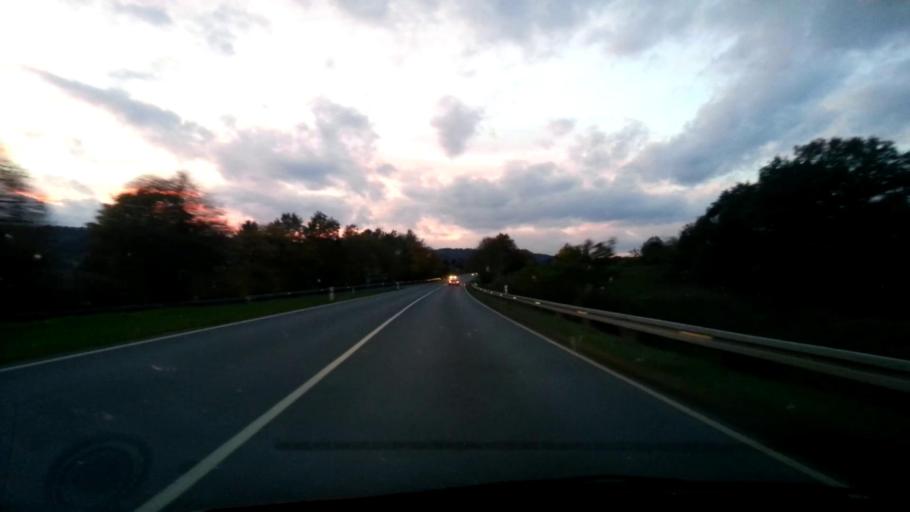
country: DE
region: Bavaria
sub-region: Upper Franconia
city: Seybothenreuth
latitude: 49.9464
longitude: 11.7214
